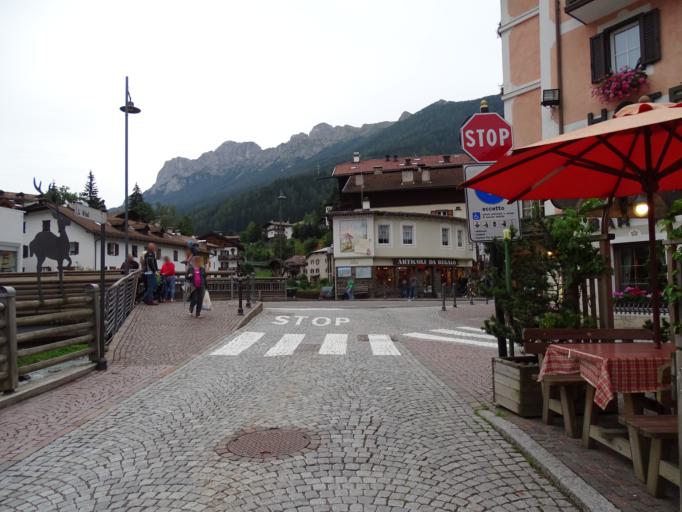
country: IT
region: Trentino-Alto Adige
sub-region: Provincia di Trento
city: Moena
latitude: 46.3763
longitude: 11.6602
